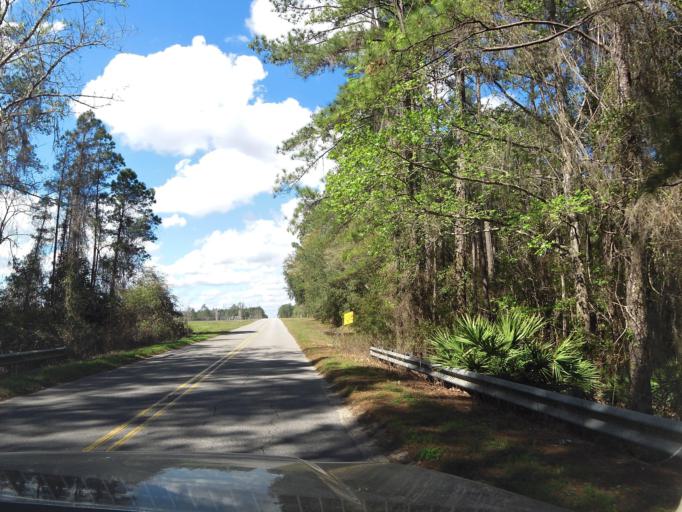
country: US
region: Florida
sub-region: Clay County
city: Green Cove Springs
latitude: 29.8681
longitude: -81.6961
